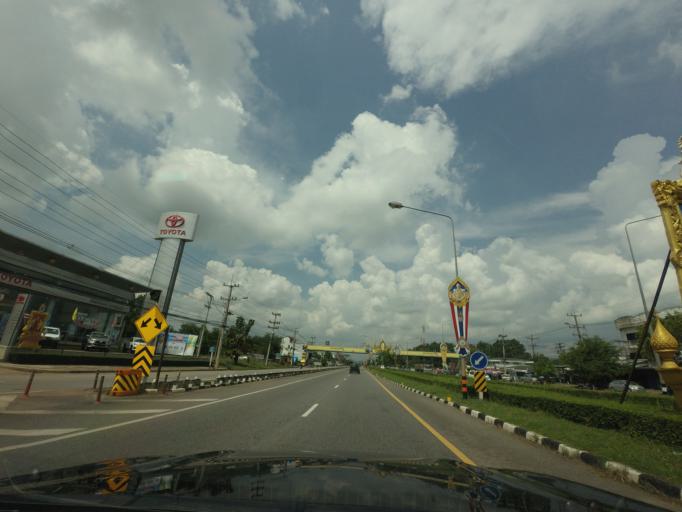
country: TH
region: Khon Kaen
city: Nong Ruea
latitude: 16.4903
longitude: 102.4443
